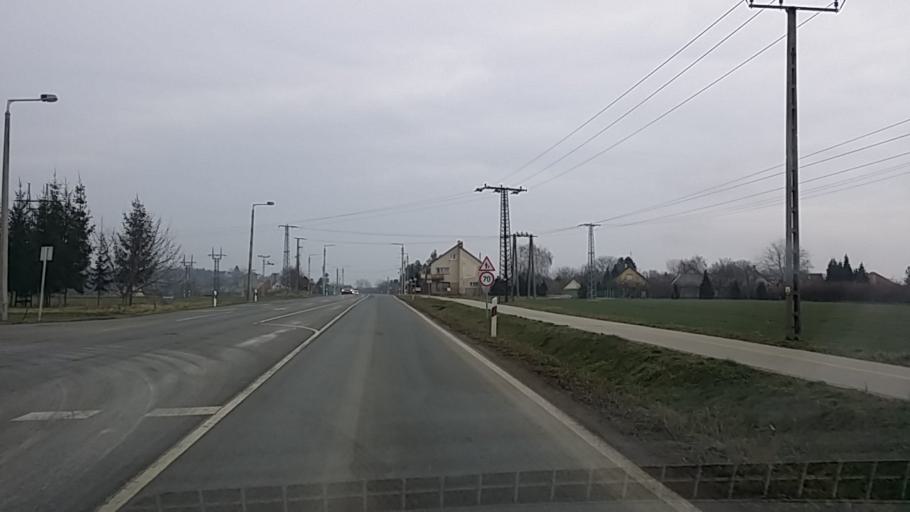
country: HU
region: Baranya
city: Mohacs
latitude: 46.0299
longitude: 18.6780
